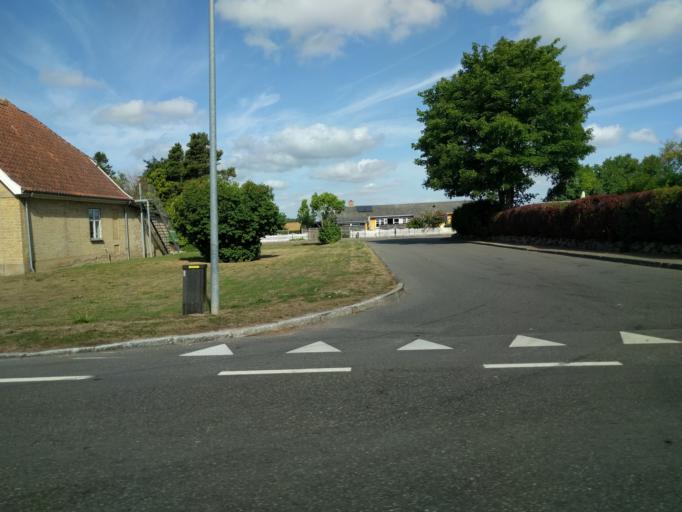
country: DK
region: Zealand
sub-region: Vordingborg Kommune
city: Stege
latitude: 54.9459
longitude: 12.2305
